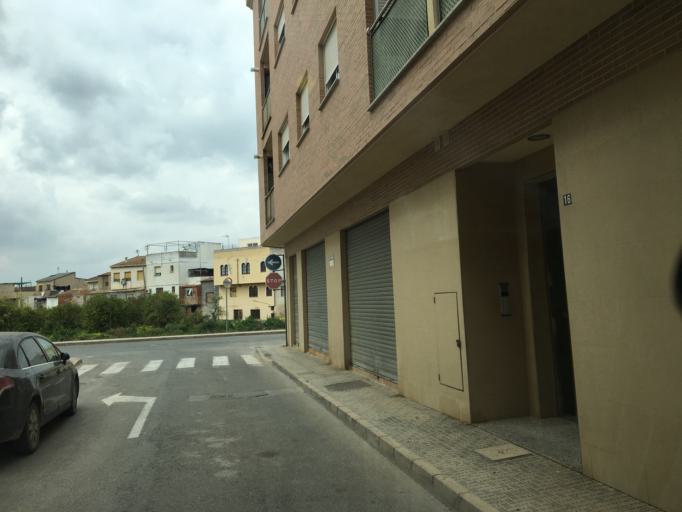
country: ES
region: Murcia
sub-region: Murcia
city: Beniel
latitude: 38.0474
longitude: -1.0052
